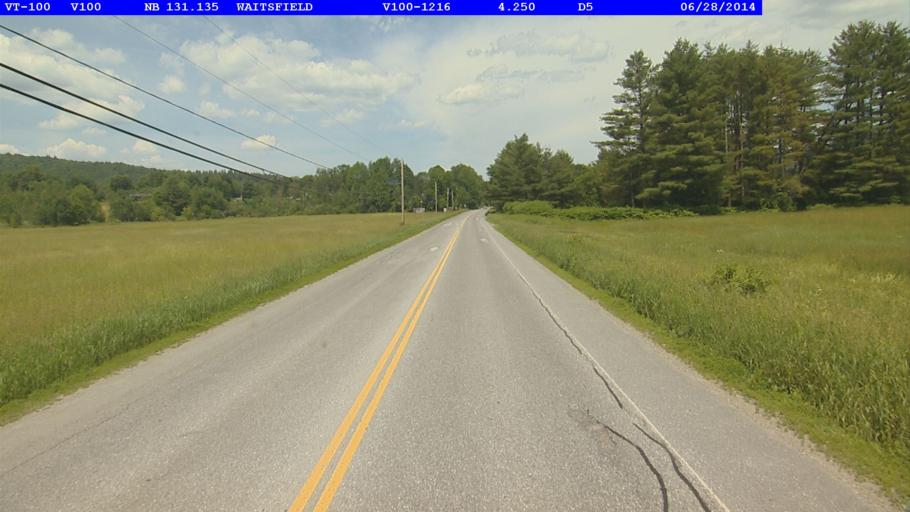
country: US
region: Vermont
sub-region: Washington County
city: Waterbury
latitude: 44.1972
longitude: -72.8174
